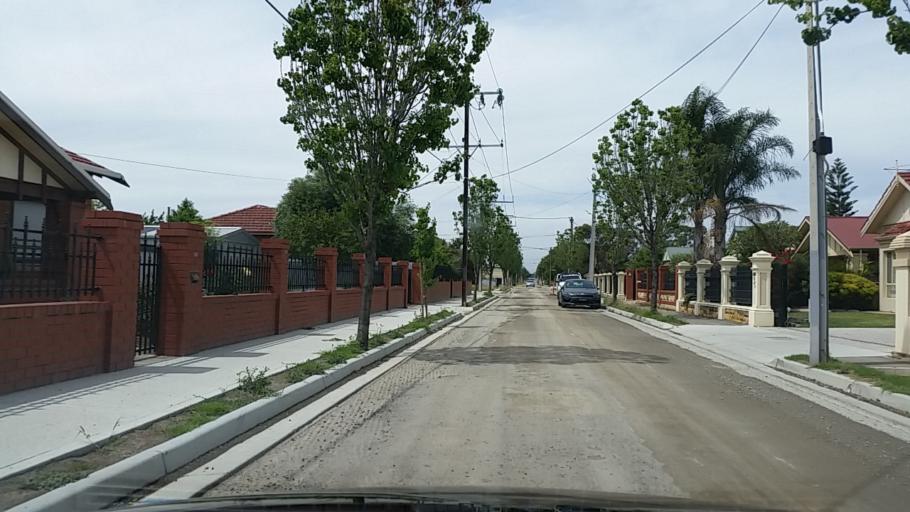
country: AU
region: South Australia
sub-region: Charles Sturt
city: Woodville
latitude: -34.8851
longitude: 138.5537
